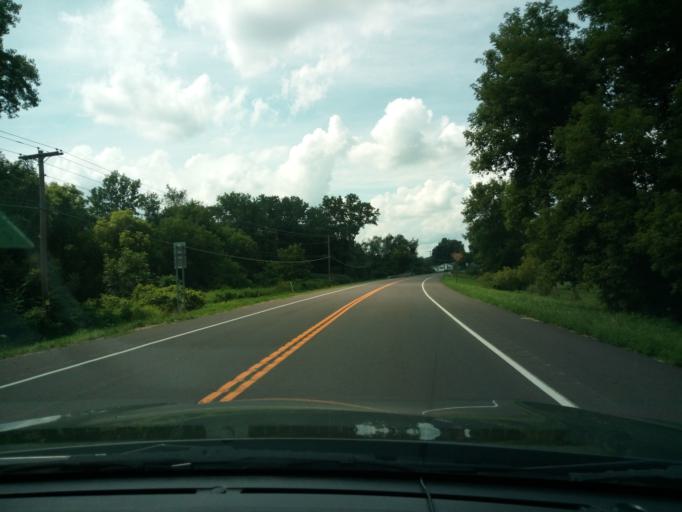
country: US
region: New York
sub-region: Chemung County
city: Southport
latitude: 42.0509
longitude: -76.7776
